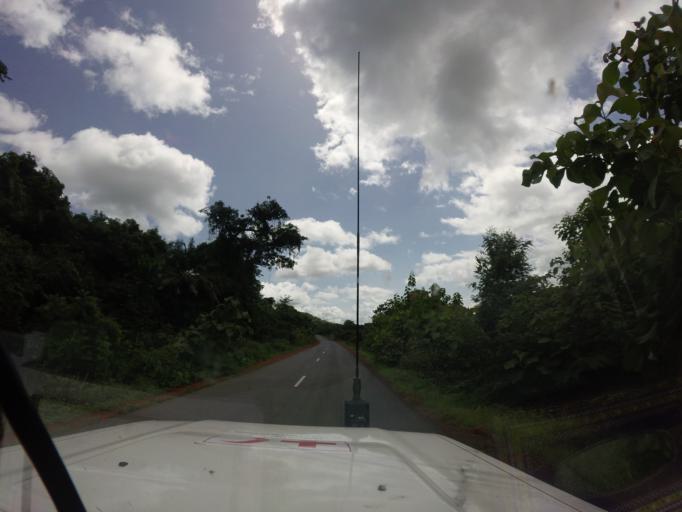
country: SL
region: Northern Province
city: Bindi
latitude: 10.1814
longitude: -11.7304
